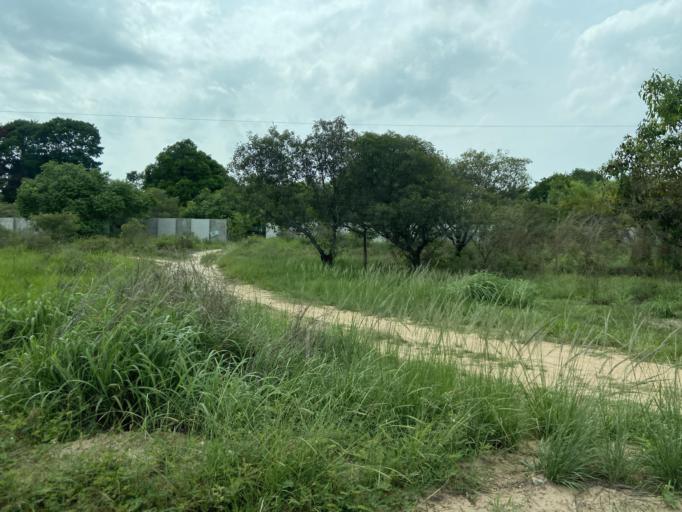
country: BR
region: Para
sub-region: Maraba
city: Maraba
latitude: -5.2923
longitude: -49.0620
